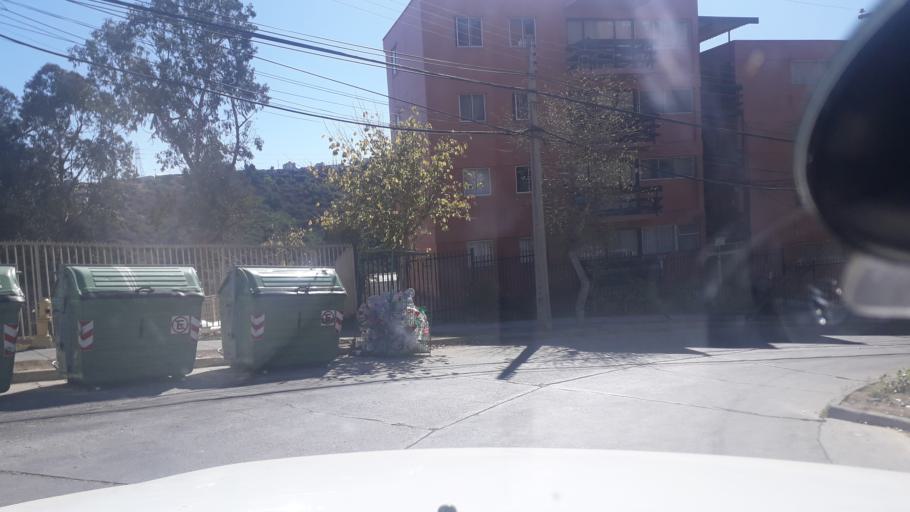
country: CL
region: Valparaiso
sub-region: Provincia de Valparaiso
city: Vina del Mar
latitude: -33.0376
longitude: -71.5155
